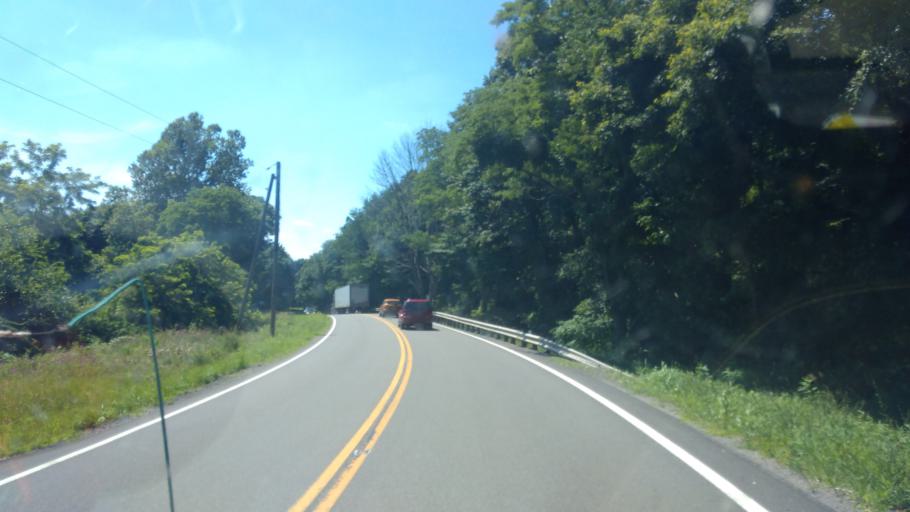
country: US
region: Ohio
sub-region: Carroll County
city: Carrollton
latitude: 40.5177
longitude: -80.9970
